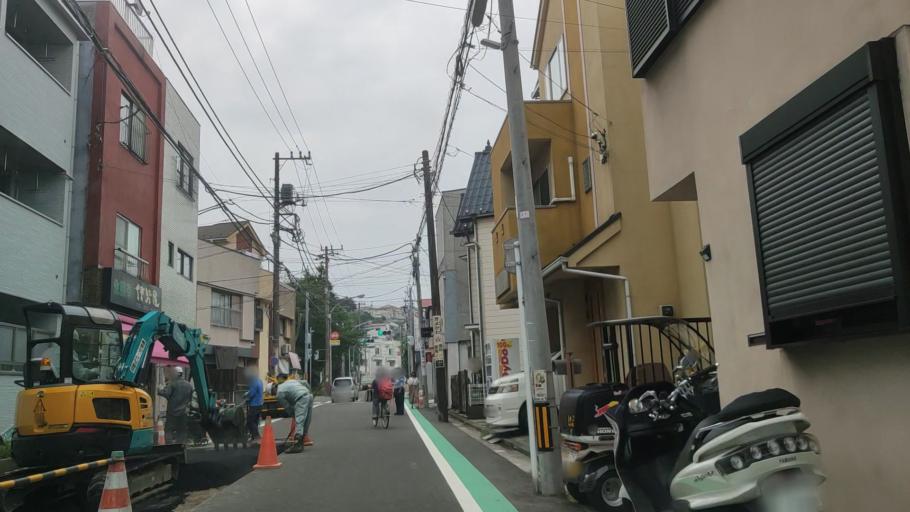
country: JP
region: Kanagawa
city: Yokohama
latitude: 35.4499
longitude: 139.6104
